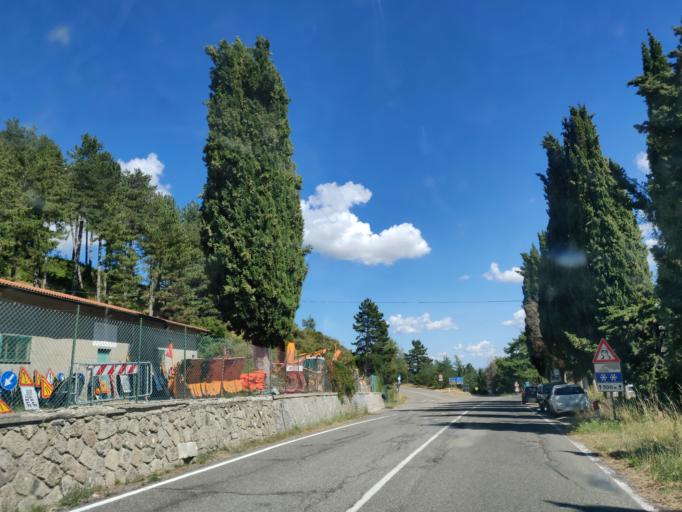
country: IT
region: Tuscany
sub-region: Provincia di Siena
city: Abbadia San Salvatore
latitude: 42.9095
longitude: 11.6720
